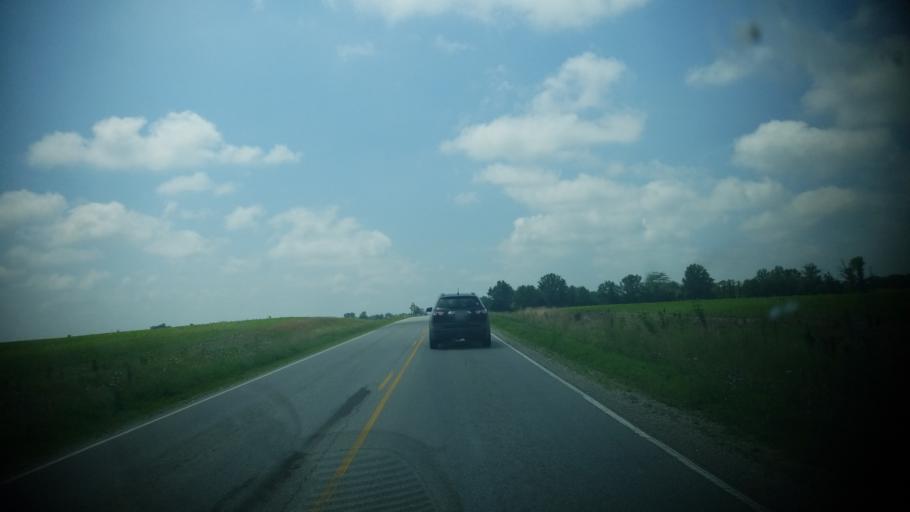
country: US
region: Illinois
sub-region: Wayne County
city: Fairfield
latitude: 38.5114
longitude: -88.3484
